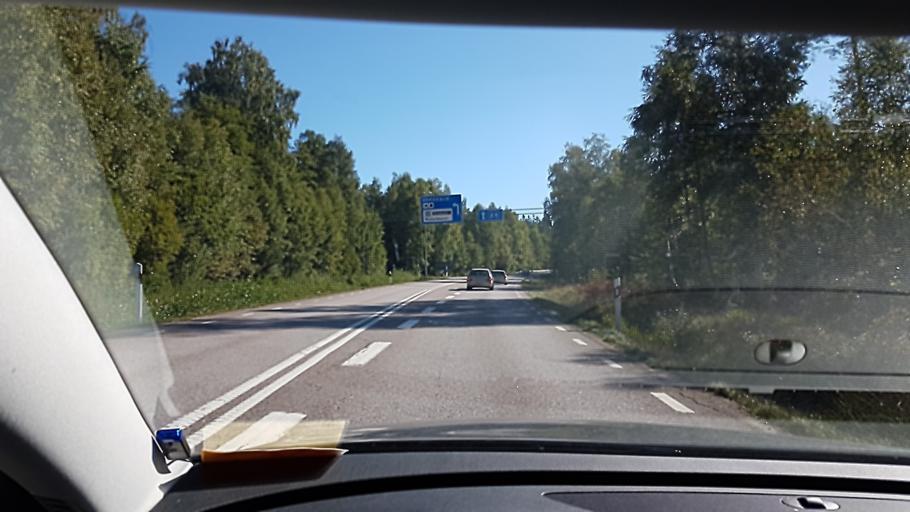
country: SE
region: Kronoberg
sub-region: Lessebo Kommun
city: Hovmantorp
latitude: 56.7869
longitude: 15.1804
